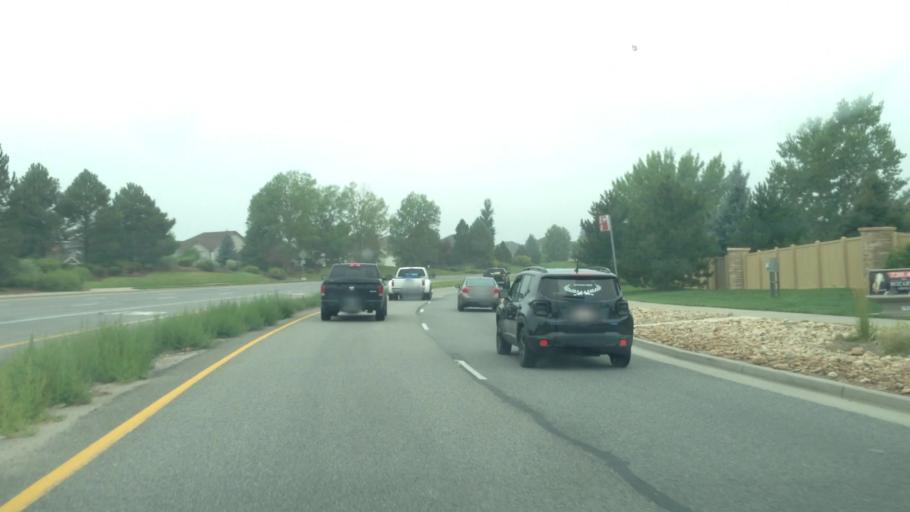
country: US
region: Colorado
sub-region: Douglas County
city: Parker
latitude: 39.6012
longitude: -104.7230
